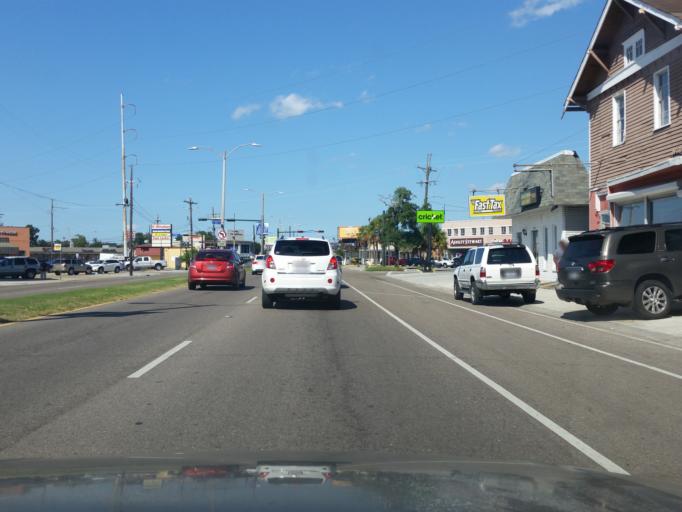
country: US
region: Louisiana
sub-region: Orleans Parish
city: New Orleans
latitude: 29.9973
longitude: -90.0611
